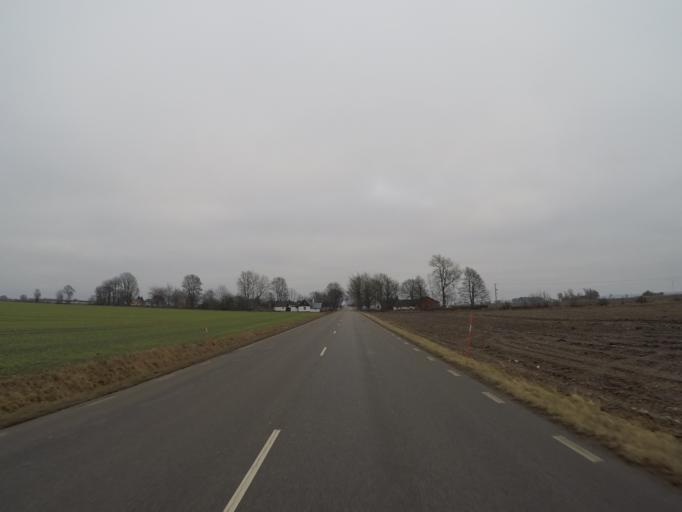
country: SE
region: Skane
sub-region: Hoors Kommun
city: Loberod
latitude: 55.7786
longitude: 13.4258
